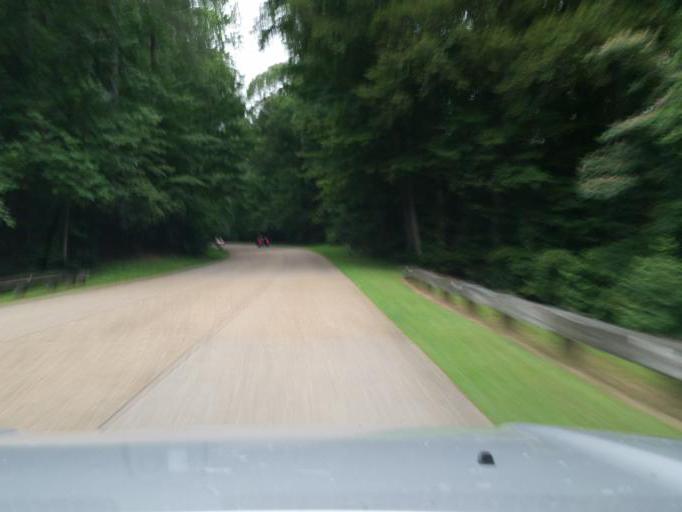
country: US
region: Virginia
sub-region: City of Williamsburg
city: Williamsburg
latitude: 37.2834
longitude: -76.6429
